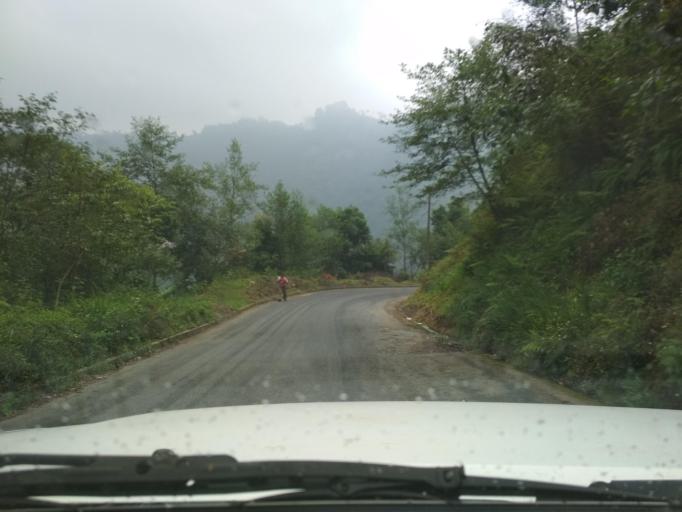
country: MX
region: Veracruz
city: La Perla
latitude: 18.9389
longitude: -97.1472
